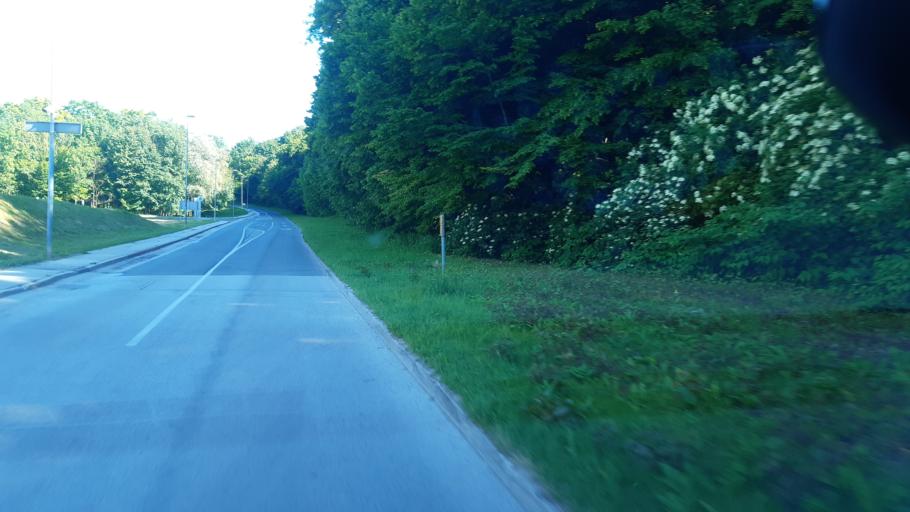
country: SI
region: Kranj
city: Kranj
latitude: 46.2205
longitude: 14.3673
